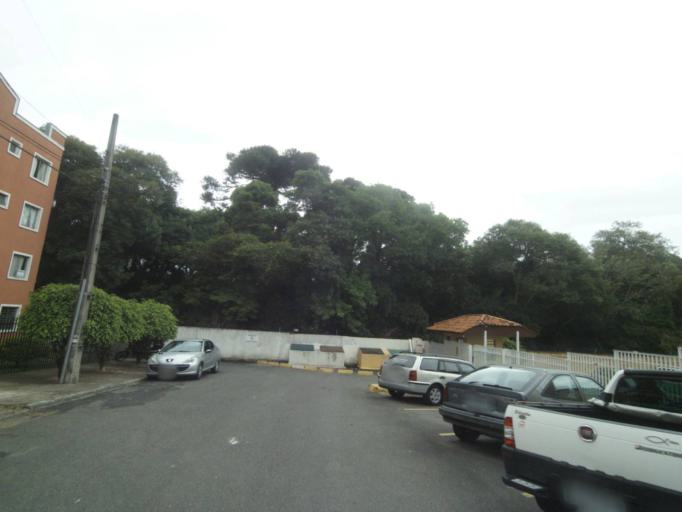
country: BR
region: Parana
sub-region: Curitiba
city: Curitiba
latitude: -25.4590
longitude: -49.3233
